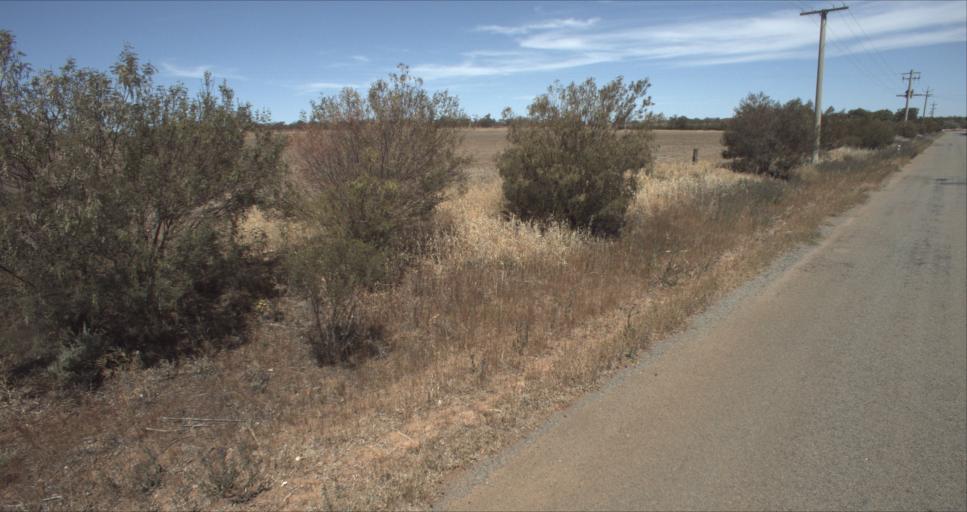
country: AU
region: New South Wales
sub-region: Leeton
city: Leeton
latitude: -34.5920
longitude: 146.4406
